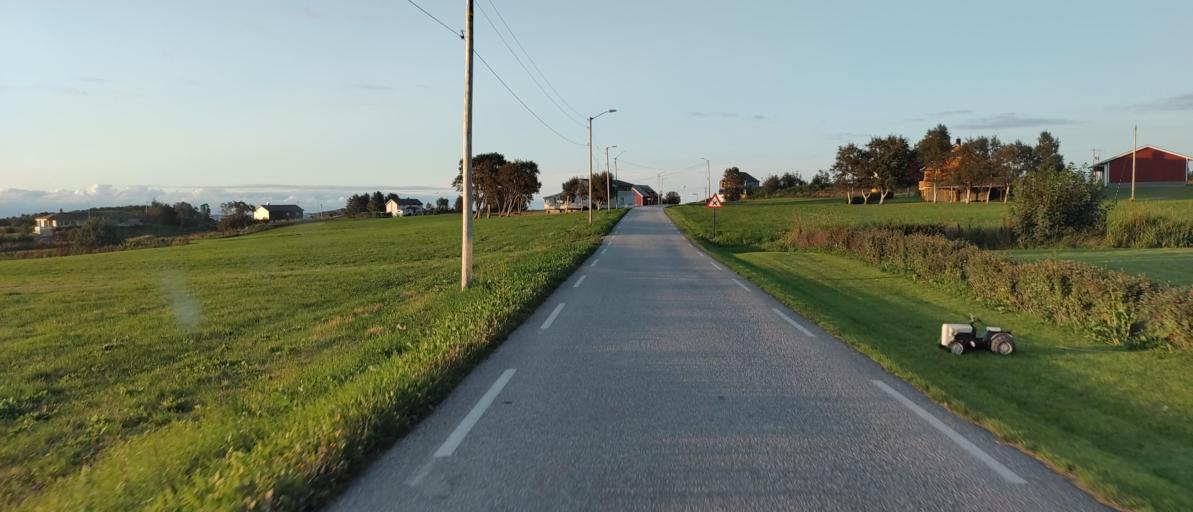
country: NO
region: More og Romsdal
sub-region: Fraena
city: Elnesvagen
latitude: 62.9957
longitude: 7.2216
